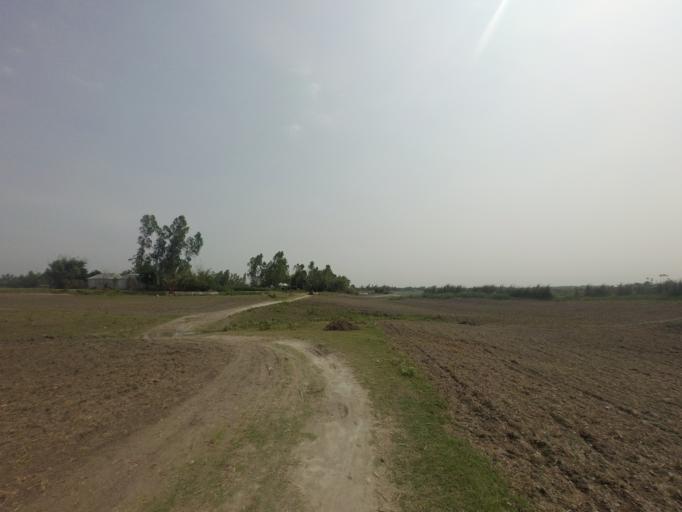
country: BD
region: Rajshahi
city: Sirajganj
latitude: 24.3494
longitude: 89.7279
